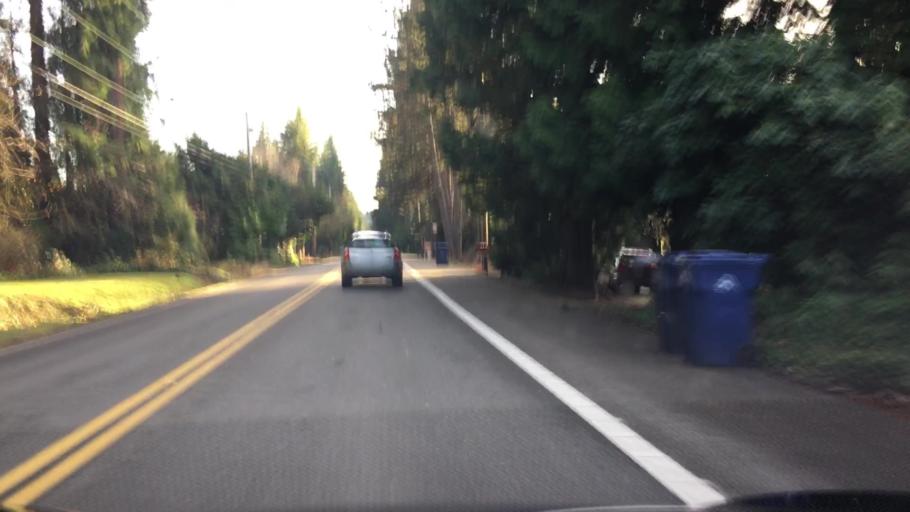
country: US
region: Washington
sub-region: Snohomish County
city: Maltby
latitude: 47.7747
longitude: -122.1318
